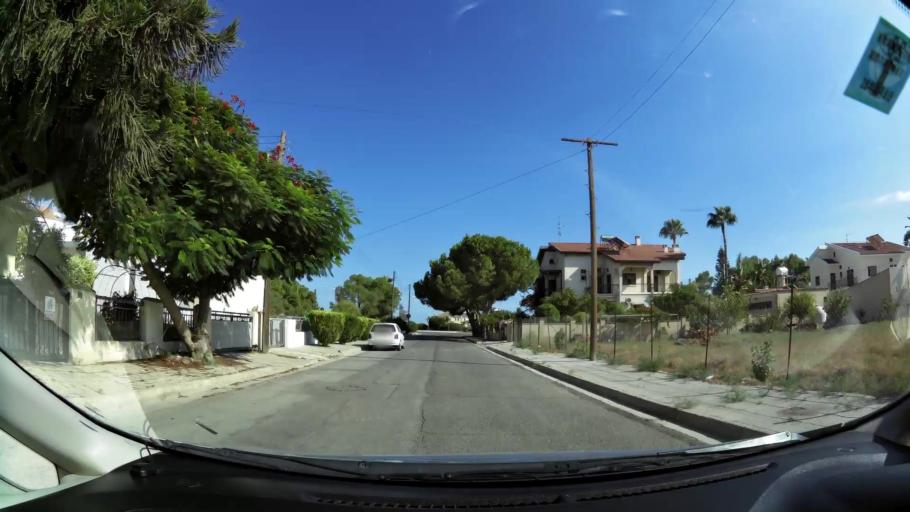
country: CY
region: Larnaka
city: Livadia
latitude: 34.9446
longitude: 33.6318
